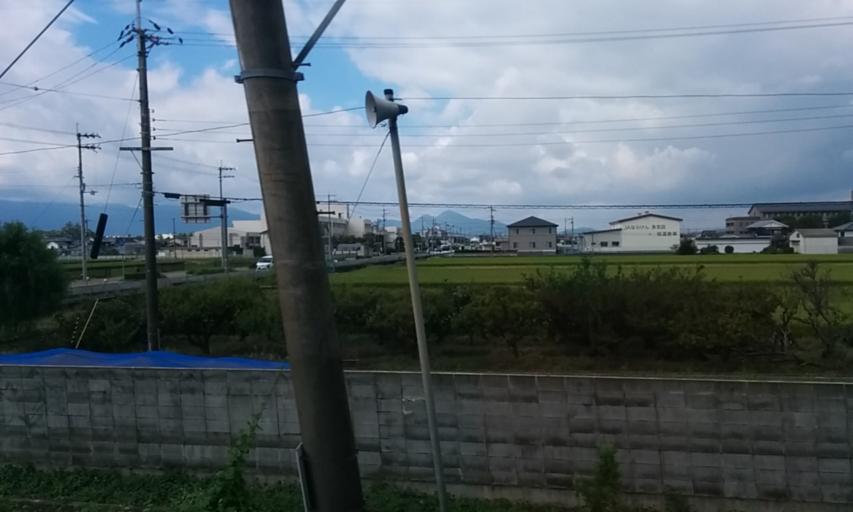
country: JP
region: Nara
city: Tawaramoto
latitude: 34.5379
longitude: 135.7939
